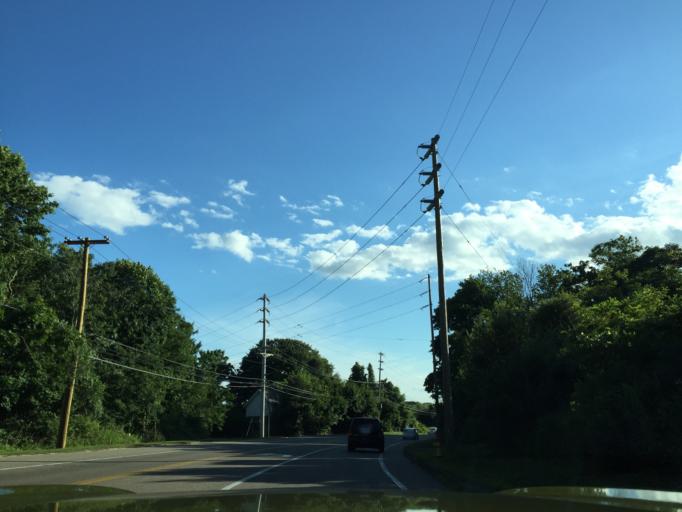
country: US
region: New York
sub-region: Suffolk County
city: Greenport West
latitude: 41.0995
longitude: -72.3896
